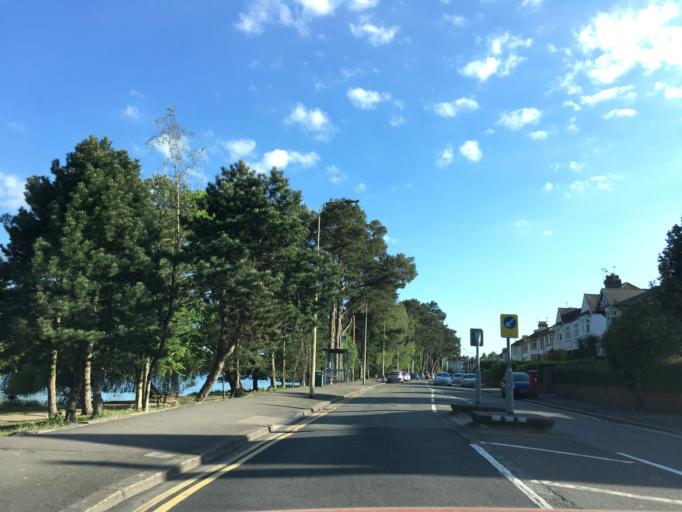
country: GB
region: Wales
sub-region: Cardiff
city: Cardiff
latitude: 51.5106
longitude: -3.1765
